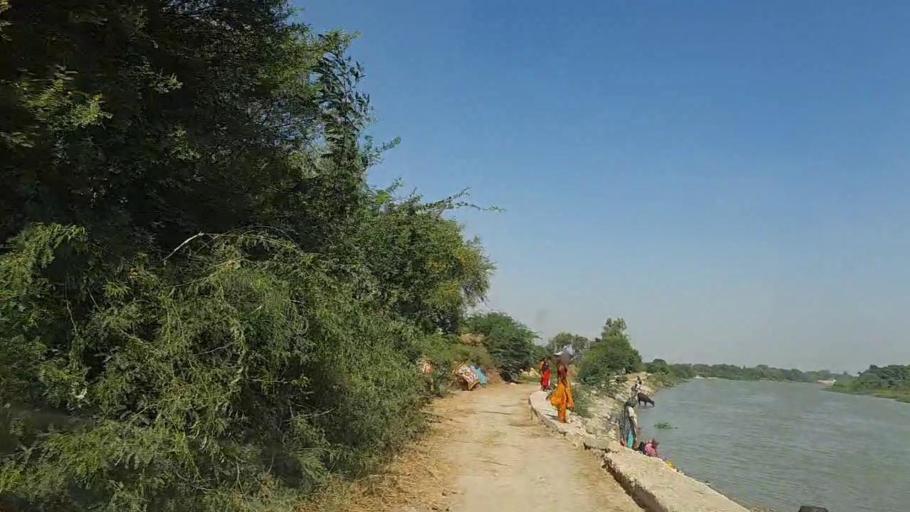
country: PK
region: Sindh
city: Daro Mehar
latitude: 24.8165
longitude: 68.1872
